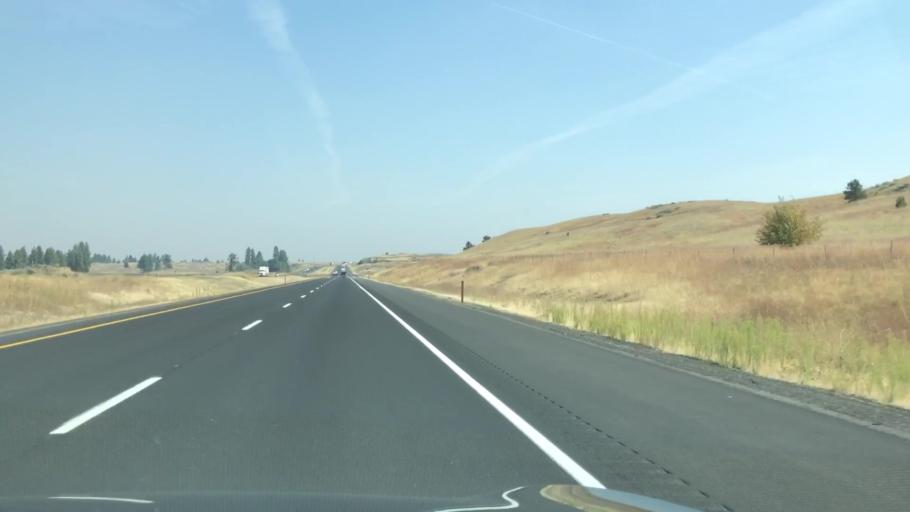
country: US
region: Washington
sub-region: Spokane County
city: Medical Lake
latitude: 47.3739
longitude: -117.8734
